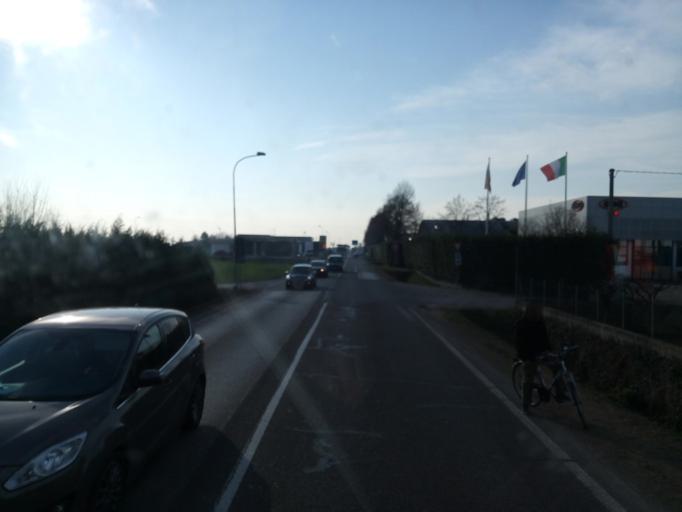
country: IT
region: Veneto
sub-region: Provincia di Vicenza
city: Brendola
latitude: 45.4896
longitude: 11.4260
